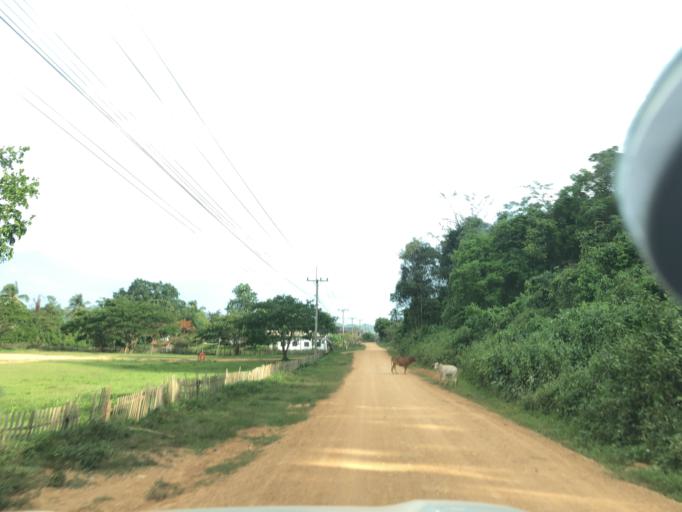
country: TH
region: Loei
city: Chiang Khan
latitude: 18.0202
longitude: 101.4187
